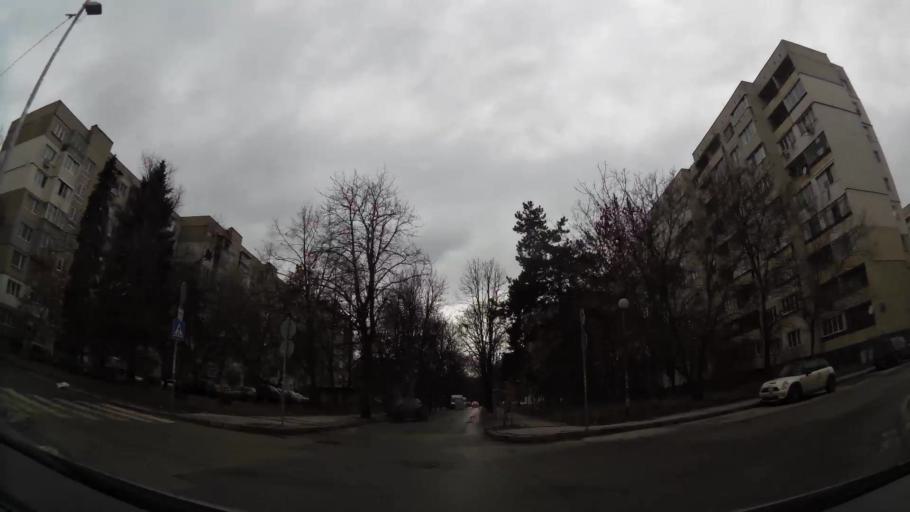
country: BG
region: Sofia-Capital
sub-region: Stolichna Obshtina
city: Sofia
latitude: 42.7265
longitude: 23.2982
